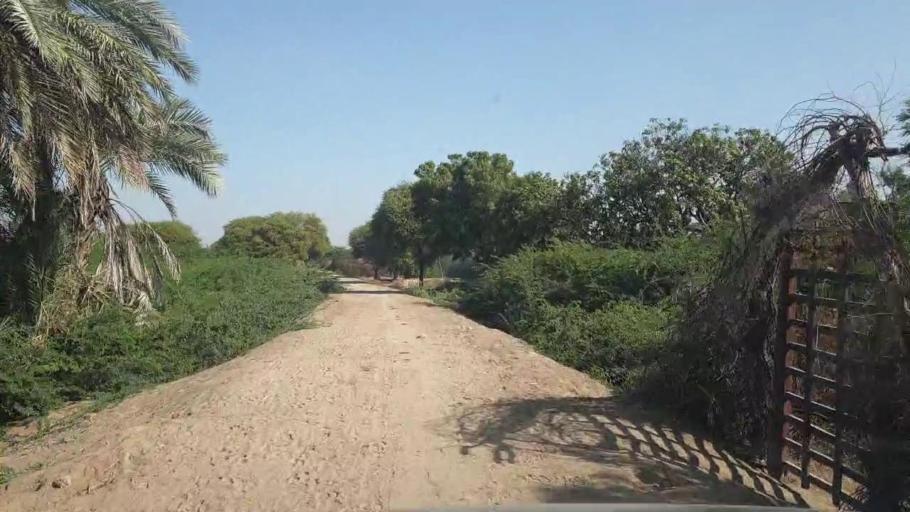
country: PK
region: Sindh
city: Talhar
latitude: 24.7823
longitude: 68.8079
